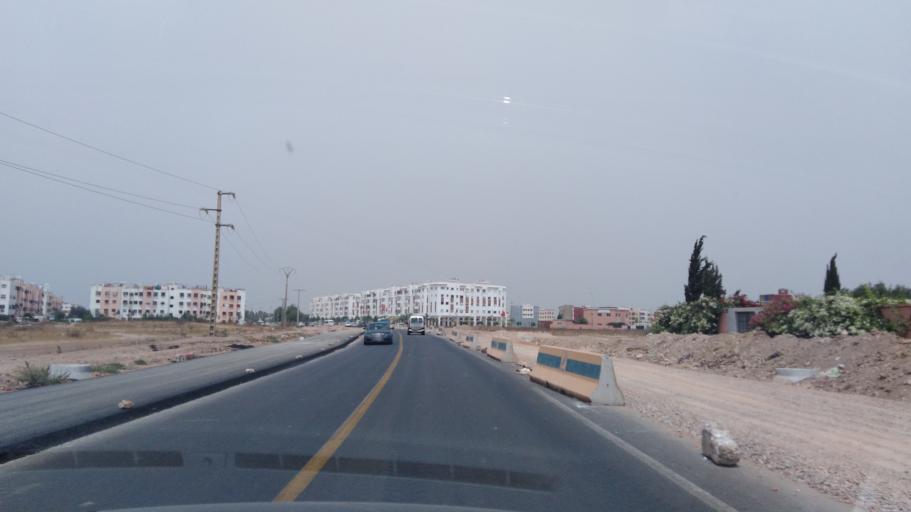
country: MA
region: Chaouia-Ouardigha
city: Nouaseur
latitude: 33.3601
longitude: -7.5476
